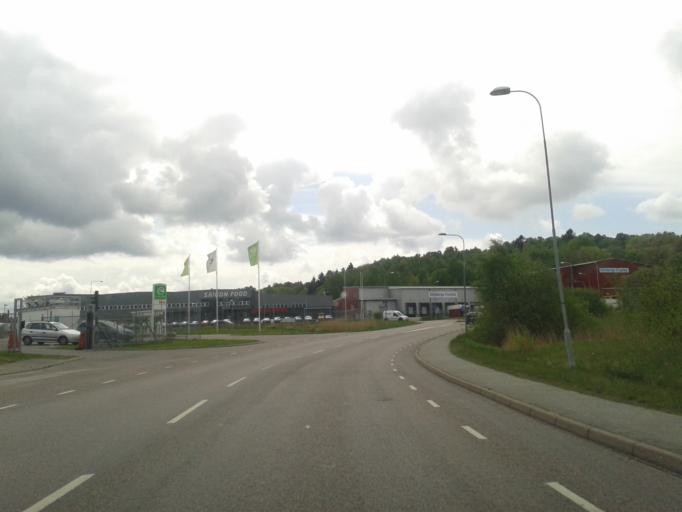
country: SE
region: Vaestra Goetaland
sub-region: Goteborg
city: Hammarkullen
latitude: 57.7893
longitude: 12.0454
